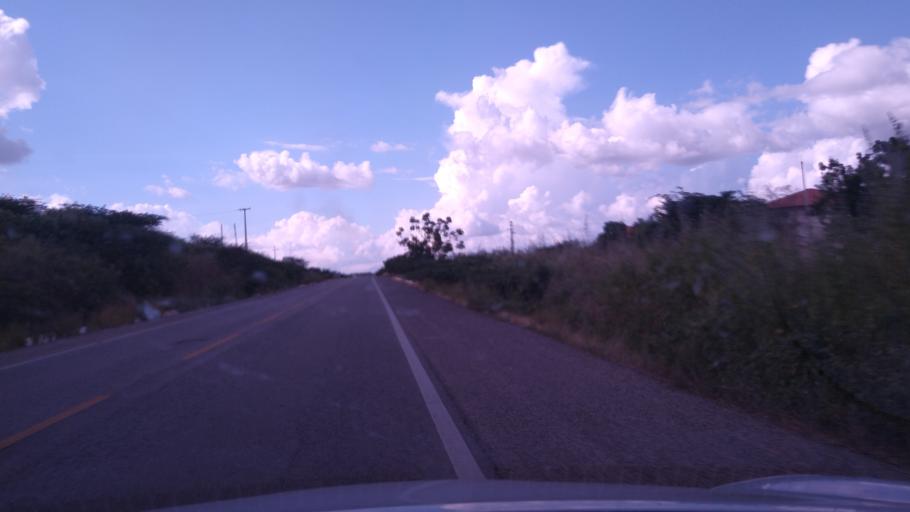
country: BR
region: Ceara
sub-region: Caninde
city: Caninde
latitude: -4.3912
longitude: -39.3136
